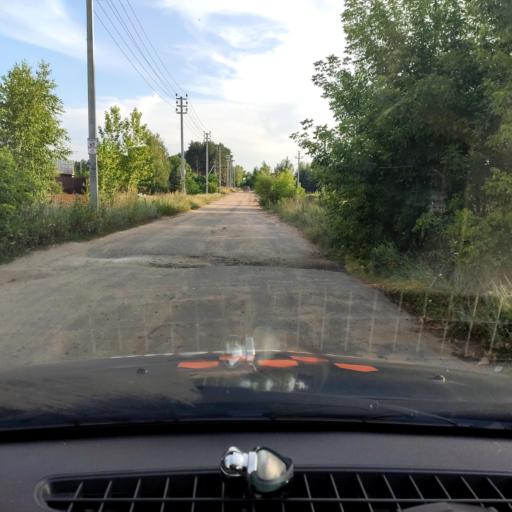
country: RU
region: Voronezj
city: Podgornoye
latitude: 51.8515
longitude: 39.1539
